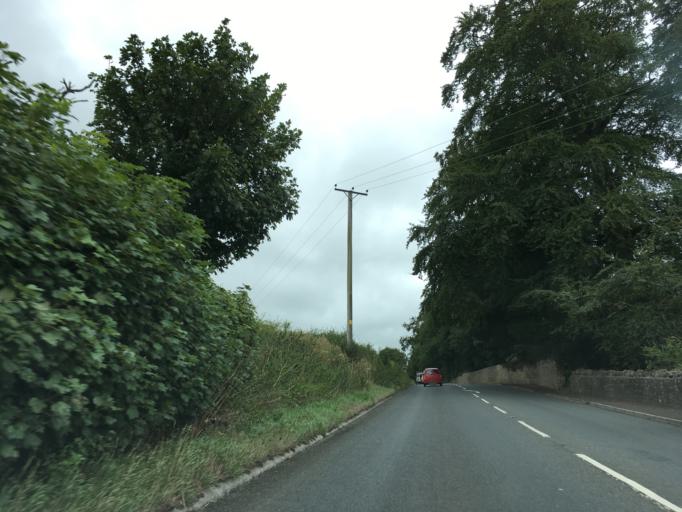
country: GB
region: England
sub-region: Bath and North East Somerset
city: Compton Dando
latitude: 51.3643
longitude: -2.4787
